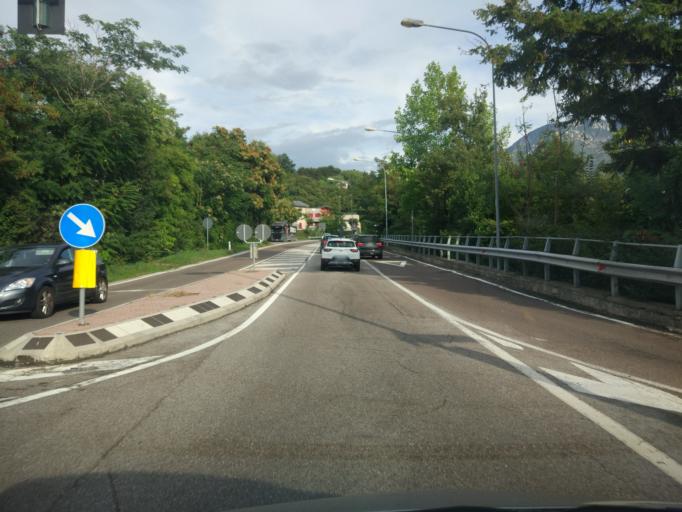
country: IT
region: Trentino-Alto Adige
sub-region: Provincia di Trento
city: Trento
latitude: 46.0774
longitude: 11.1305
